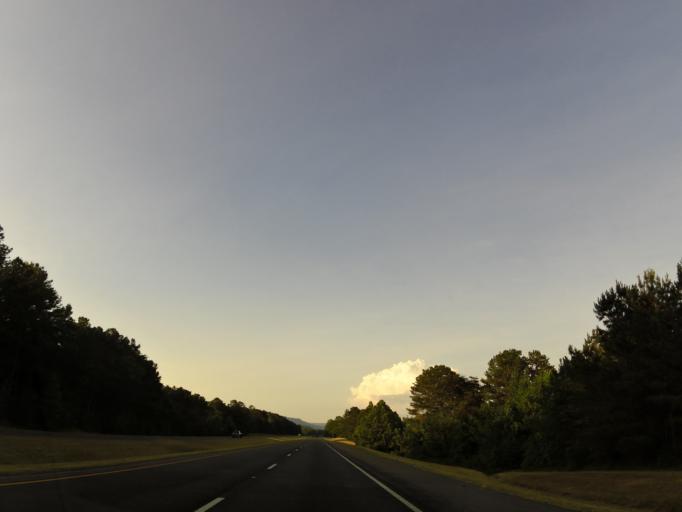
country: US
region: Alabama
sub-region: DeKalb County
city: Henagar
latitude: 34.6423
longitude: -85.6140
